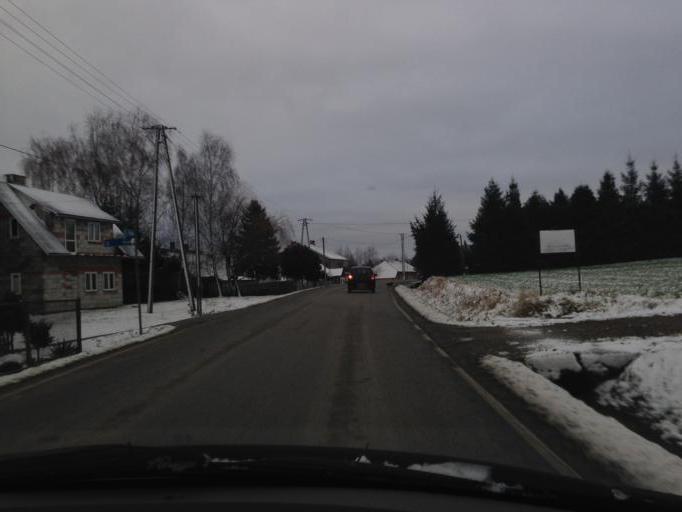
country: PL
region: Lesser Poland Voivodeship
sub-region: Powiat gorlicki
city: Moszczenica
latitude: 49.7396
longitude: 21.0889
